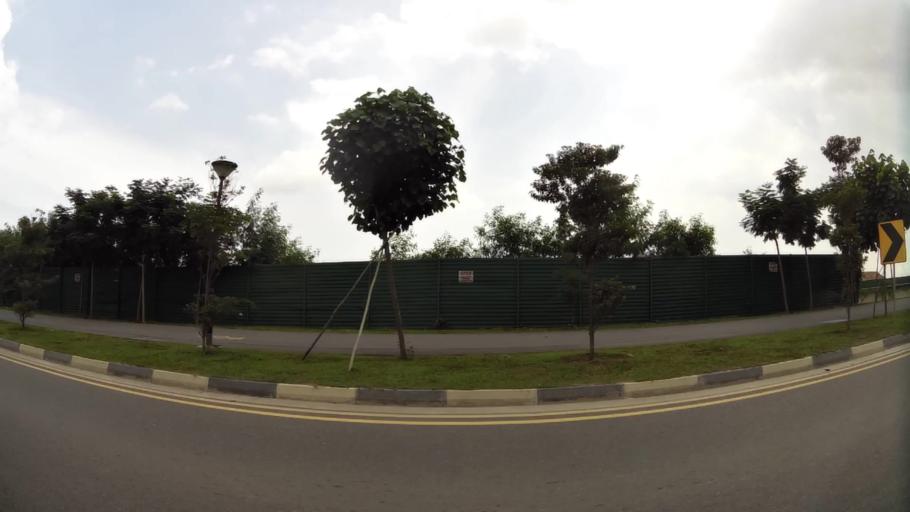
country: SG
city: Singapore
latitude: 1.3312
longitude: 103.9896
